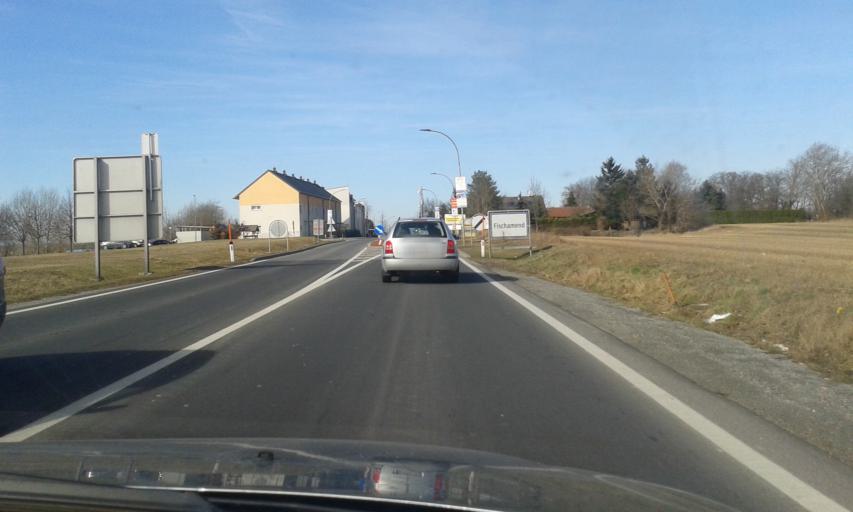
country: AT
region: Lower Austria
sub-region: Politischer Bezirk Wien-Umgebung
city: Fischamend Dorf
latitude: 48.1176
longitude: 16.6251
